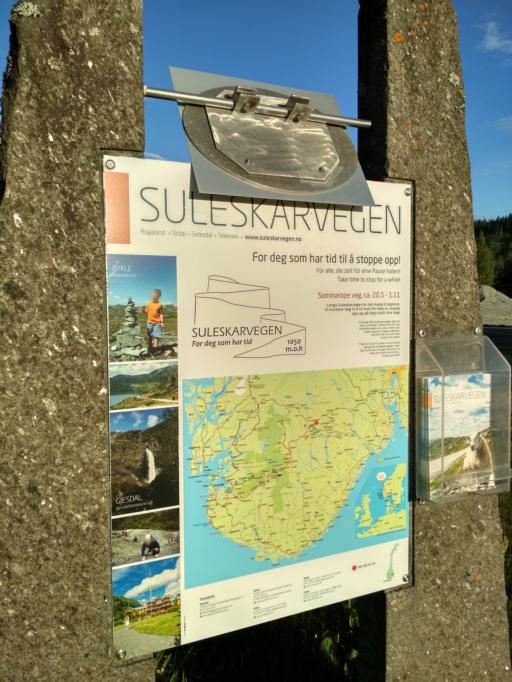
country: NO
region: Telemark
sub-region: Tokke
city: Dalen
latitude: 59.4946
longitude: 8.2032
